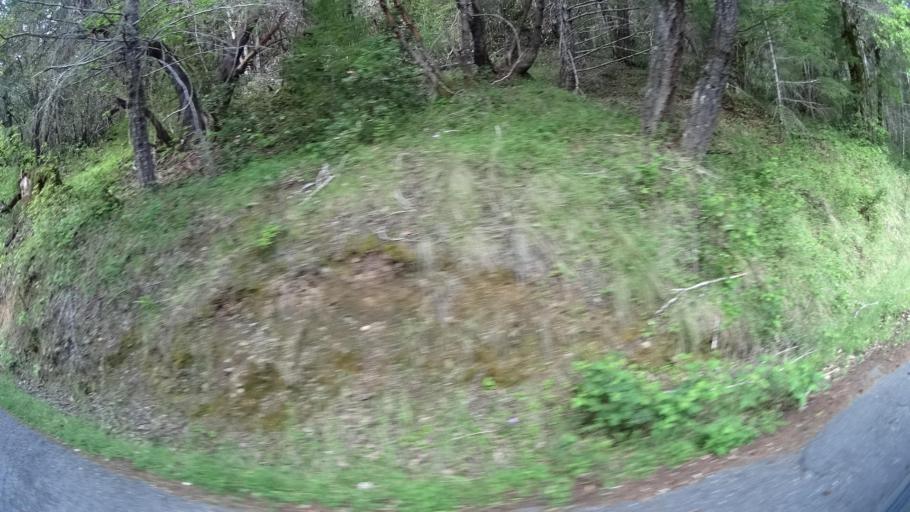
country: US
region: California
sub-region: Humboldt County
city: Redway
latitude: 40.2145
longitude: -123.6575
